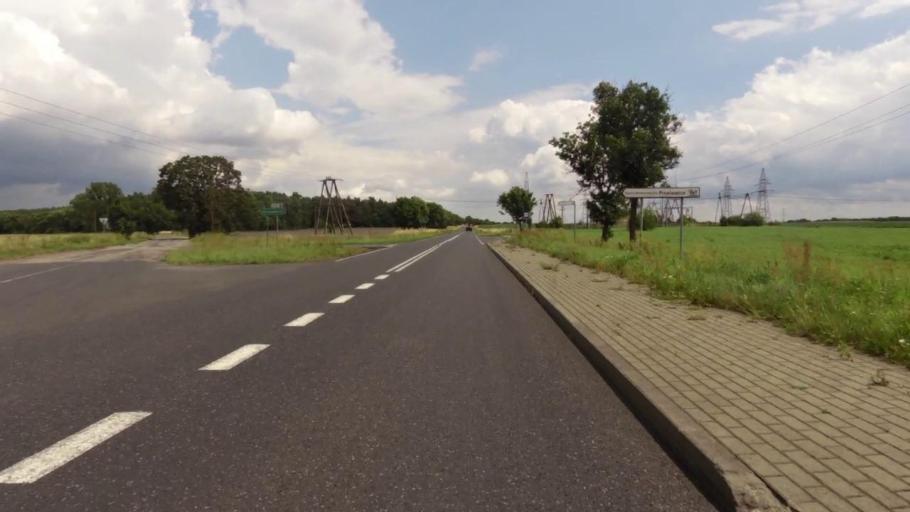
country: PL
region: West Pomeranian Voivodeship
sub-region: Powiat mysliborski
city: Nowogrodek Pomorski
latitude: 52.9958
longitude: 15.0665
